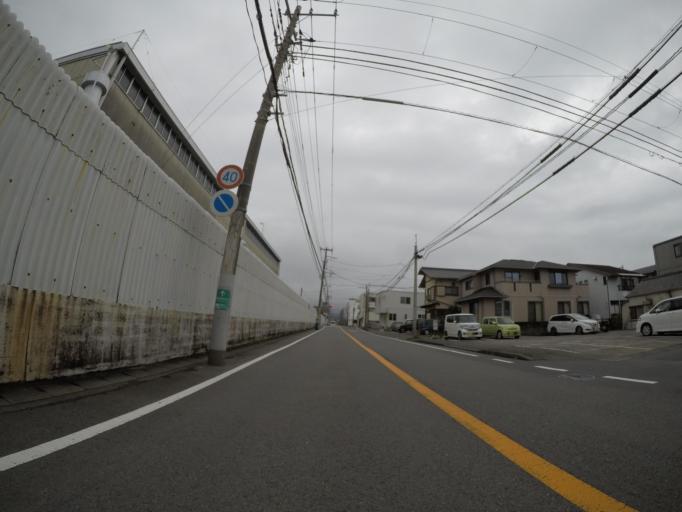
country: JP
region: Shizuoka
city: Numazu
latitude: 35.1113
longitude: 138.8521
